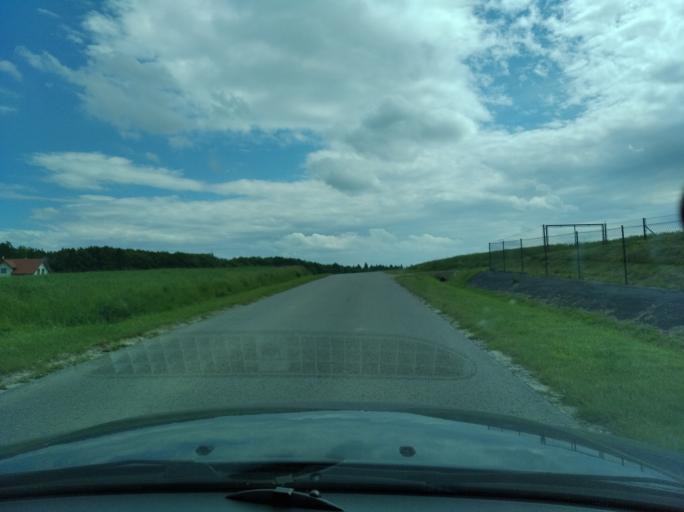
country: PL
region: Subcarpathian Voivodeship
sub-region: Powiat ropczycko-sedziszowski
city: Ropczyce
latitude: 50.0227
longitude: 21.6049
